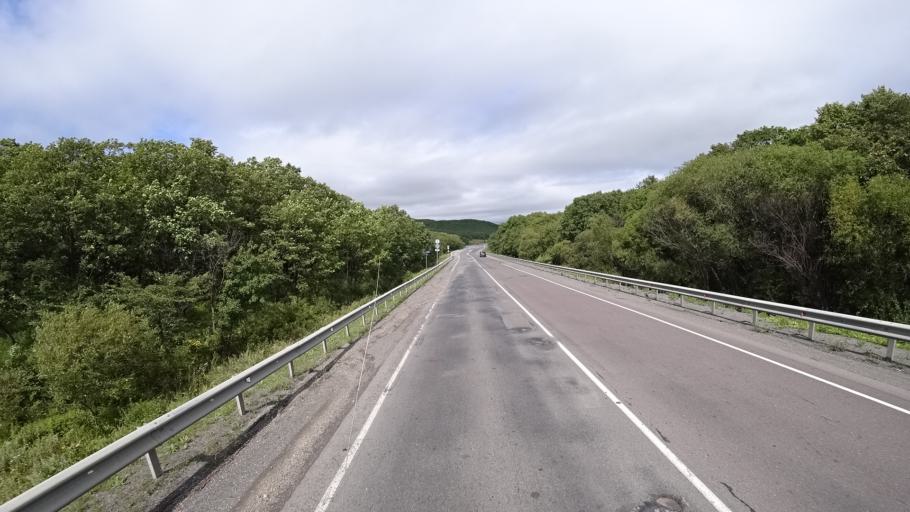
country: RU
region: Primorskiy
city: Lyalichi
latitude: 44.1354
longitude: 132.4278
